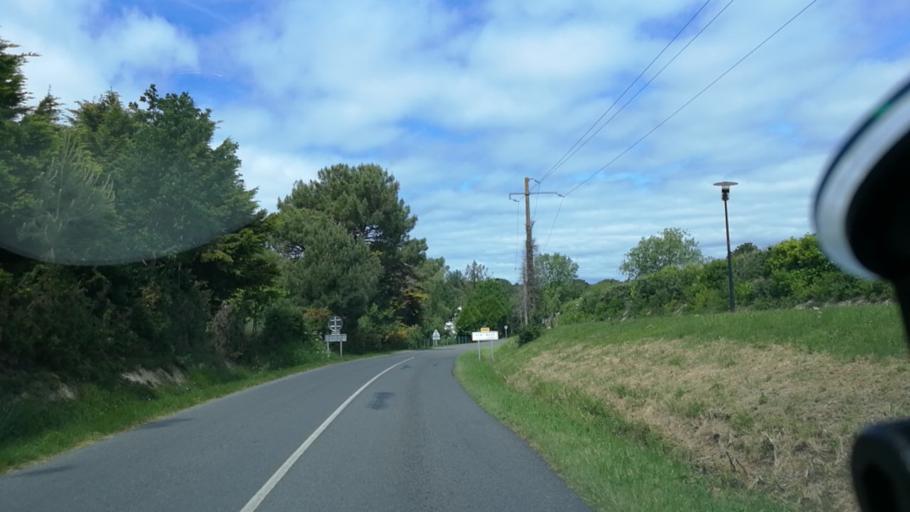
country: FR
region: Brittany
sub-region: Departement du Morbihan
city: Penestin
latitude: 47.4453
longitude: -2.4468
